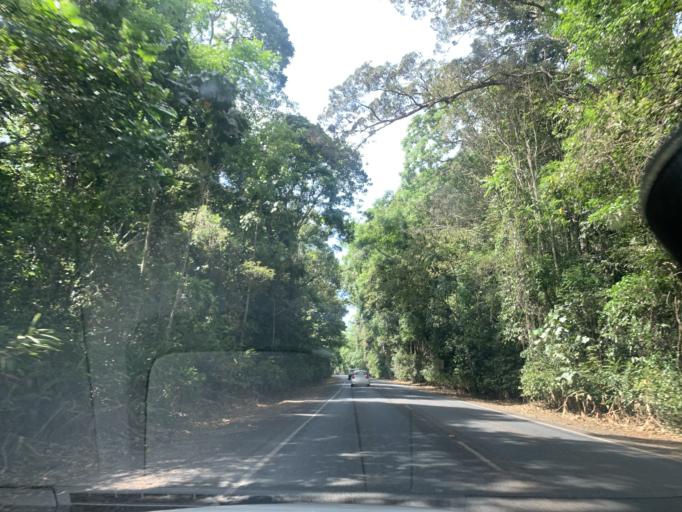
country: AU
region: Queensland
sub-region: Tablelands
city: Tolga
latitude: -17.2395
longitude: 145.4794
